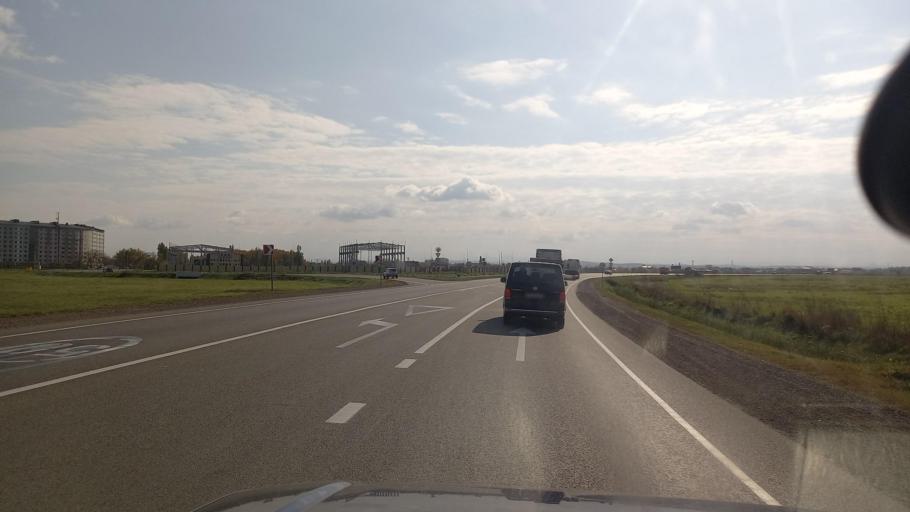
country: RU
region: Krasnodarskiy
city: Abinsk
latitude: 44.8706
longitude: 38.1279
